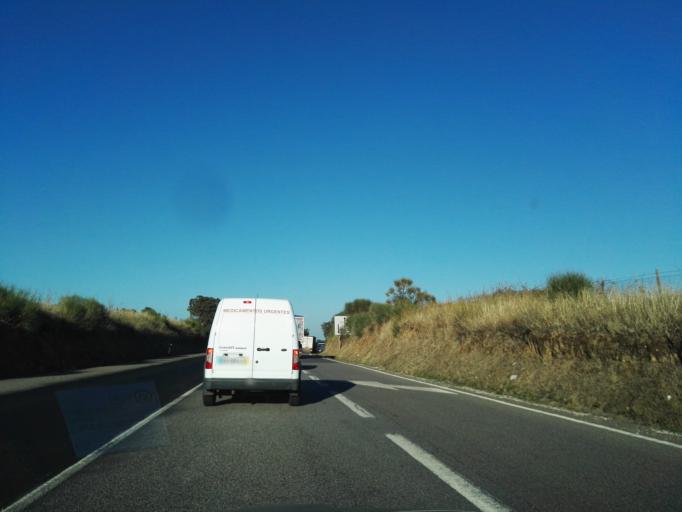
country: PT
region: Evora
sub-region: Vila Vicosa
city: Vila Vicosa
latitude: 38.8365
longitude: -7.4017
